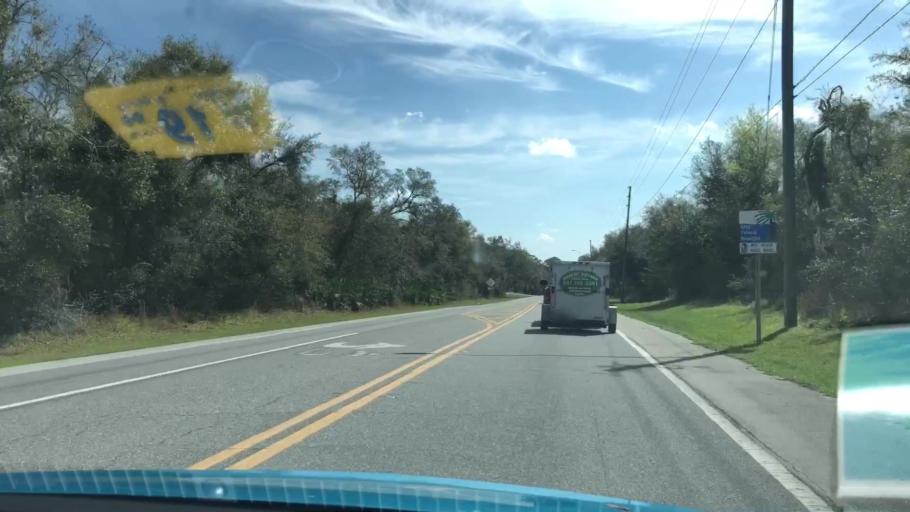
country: US
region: Florida
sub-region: Volusia County
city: Deltona
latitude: 28.8692
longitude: -81.2243
